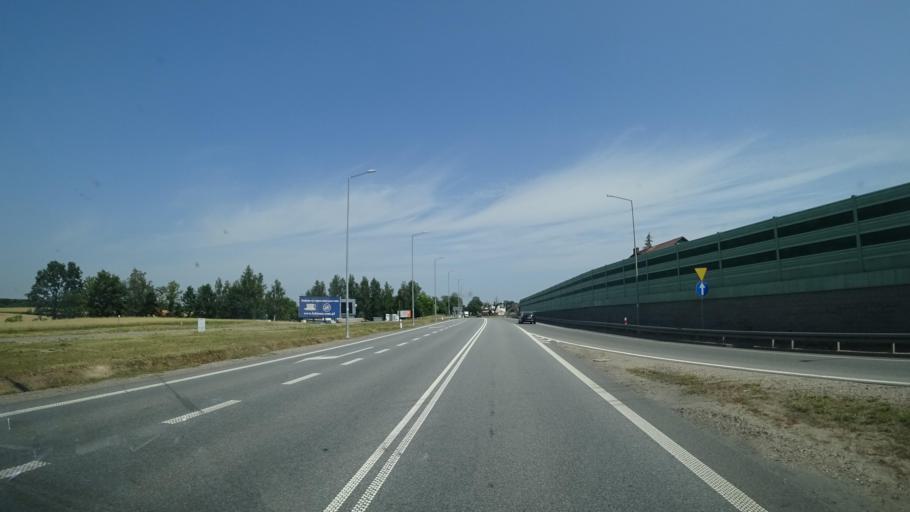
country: PL
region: Pomeranian Voivodeship
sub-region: Powiat koscierski
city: Koscierzyna
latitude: 54.1373
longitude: 18.0140
